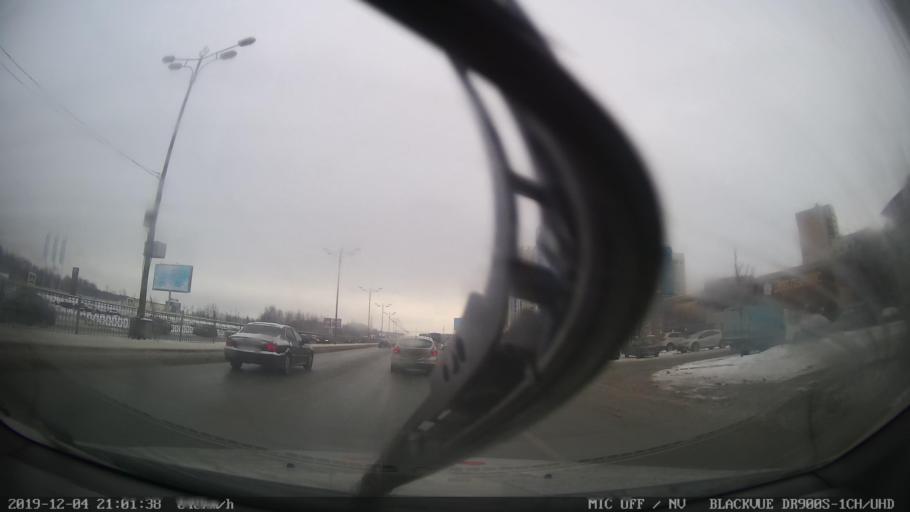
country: RU
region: Tatarstan
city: Stolbishchi
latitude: 55.7309
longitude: 49.1926
